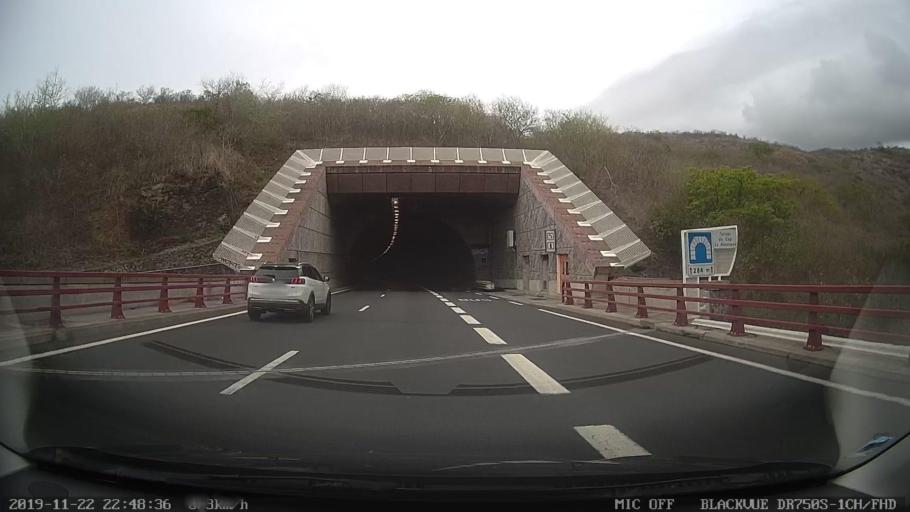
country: RE
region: Reunion
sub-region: Reunion
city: Saint-Paul
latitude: -21.0308
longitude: 55.2514
